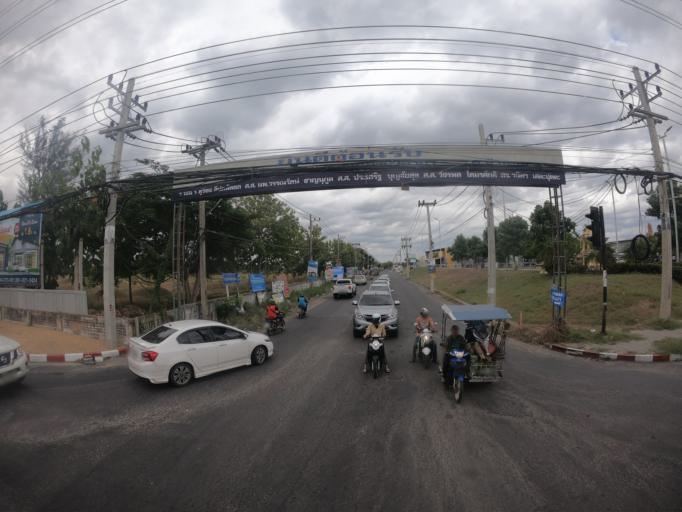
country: TH
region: Nakhon Ratchasima
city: Nakhon Ratchasima
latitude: 14.9488
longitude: 102.1255
